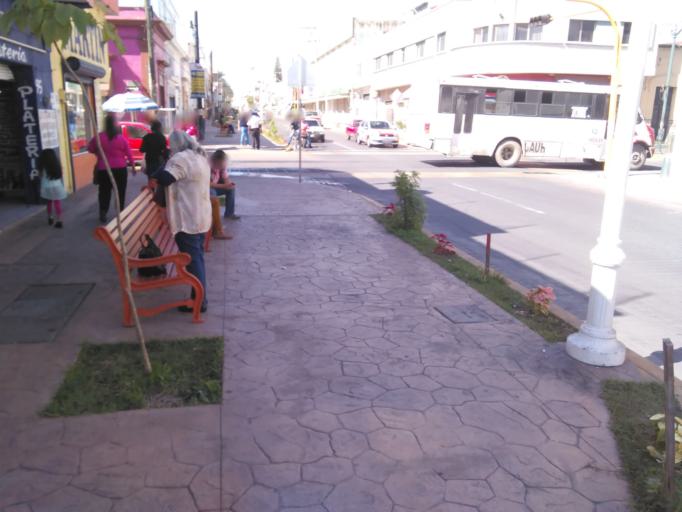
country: MX
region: Nayarit
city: Tepic
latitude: 21.5092
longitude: -104.8945
